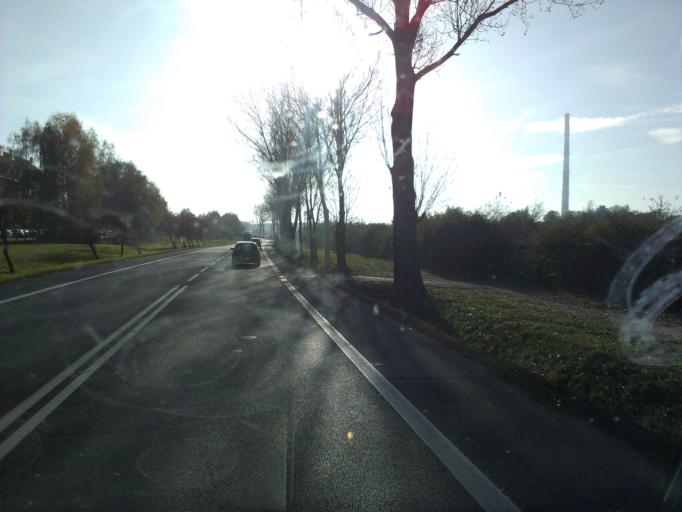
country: PL
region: Lower Silesian Voivodeship
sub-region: Powiat lubinski
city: Lubin
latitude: 51.3807
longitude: 16.1944
